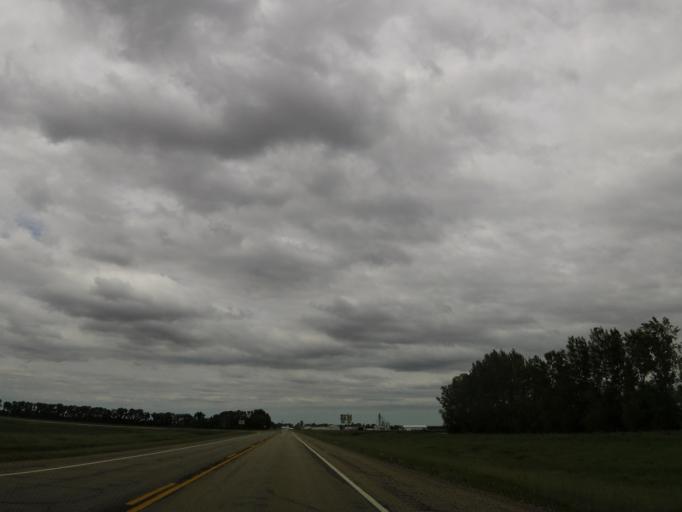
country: US
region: North Dakota
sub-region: Walsh County
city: Grafton
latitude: 48.5993
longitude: -97.4475
